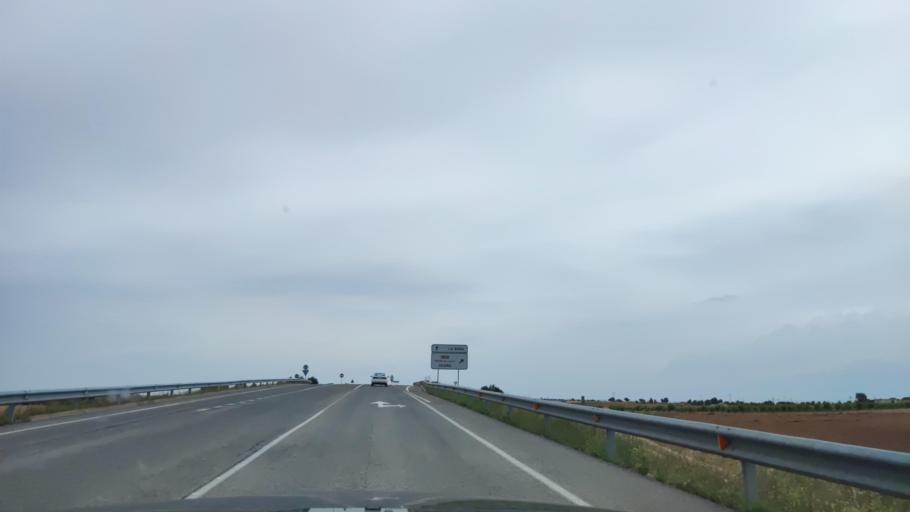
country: ES
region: Castille-La Mancha
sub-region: Provincia de Albacete
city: La Roda
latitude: 39.2228
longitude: -2.1902
